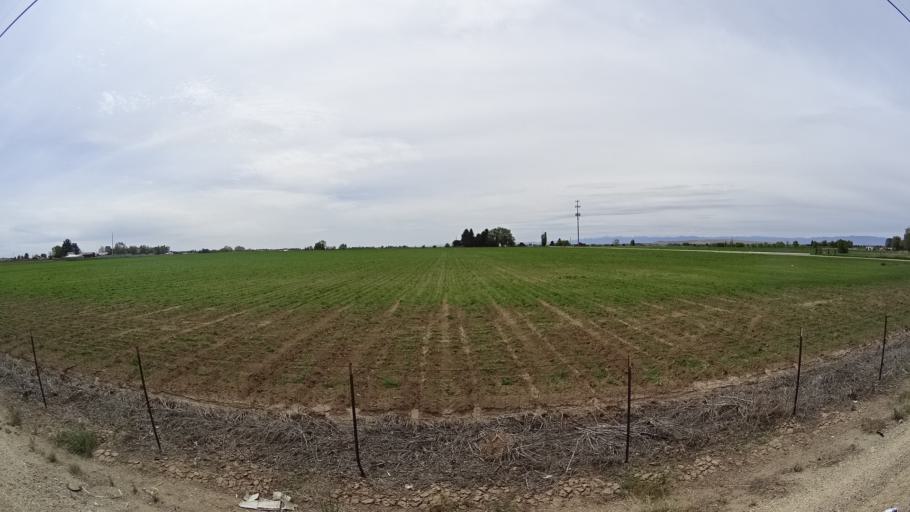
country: US
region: Idaho
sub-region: Ada County
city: Kuna
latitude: 43.5320
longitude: -116.3607
